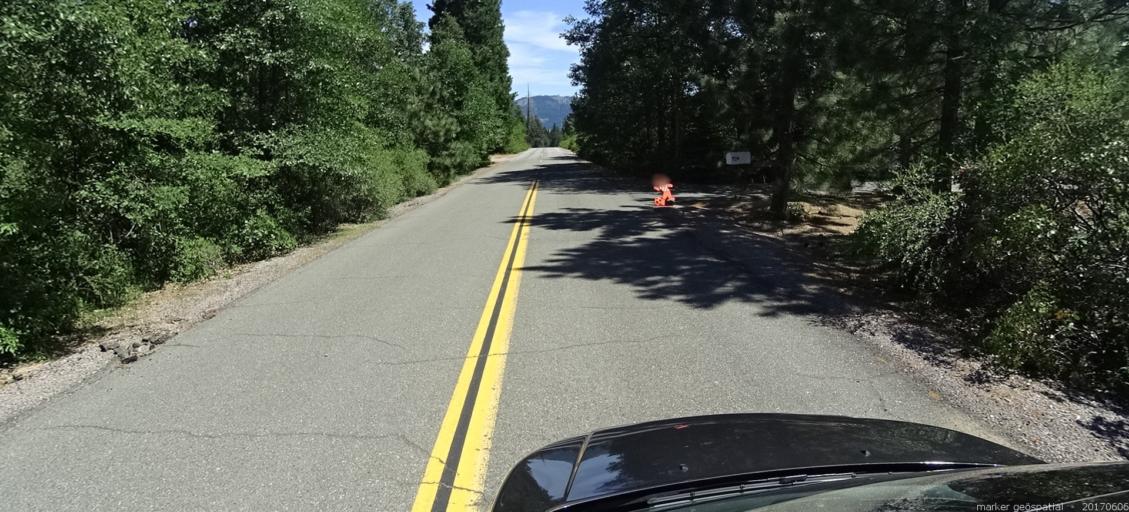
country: US
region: California
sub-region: Siskiyou County
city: Mount Shasta
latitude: 41.2827
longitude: -122.2938
